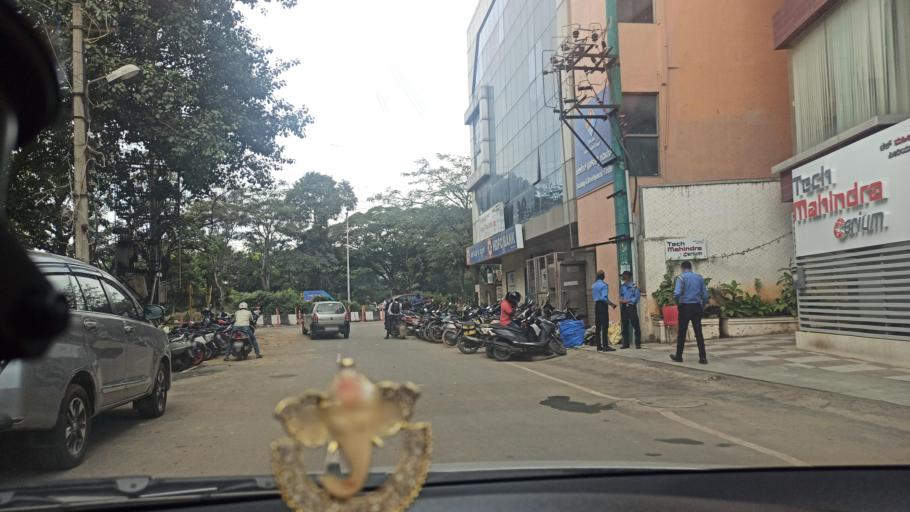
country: IN
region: Karnataka
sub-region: Bangalore Urban
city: Bangalore
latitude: 12.9229
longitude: 77.6469
